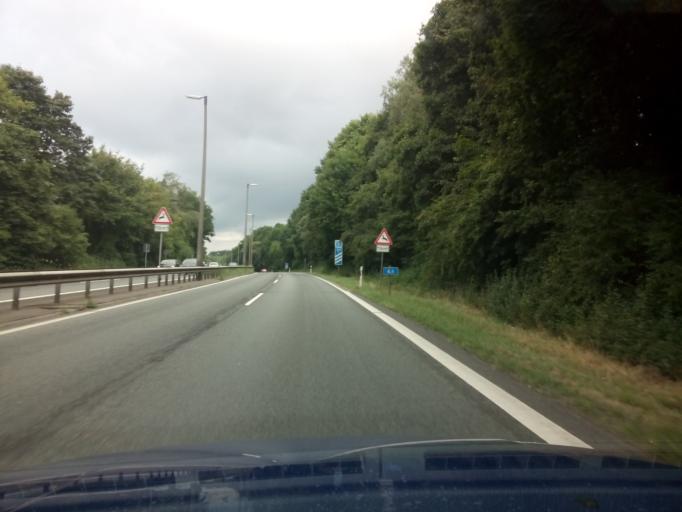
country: DE
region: Lower Saxony
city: Lemwerder
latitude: 53.1746
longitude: 8.6468
